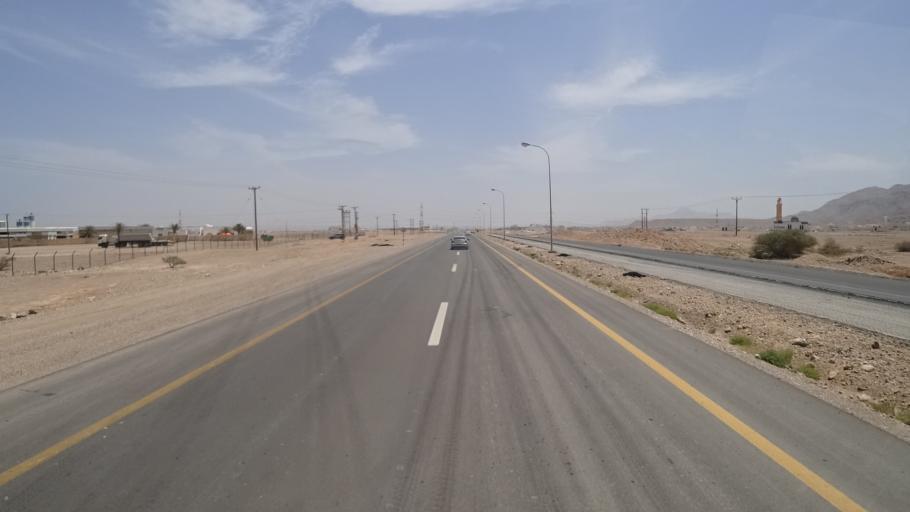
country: OM
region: Ash Sharqiyah
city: Sur
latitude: 22.6129
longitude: 59.4252
